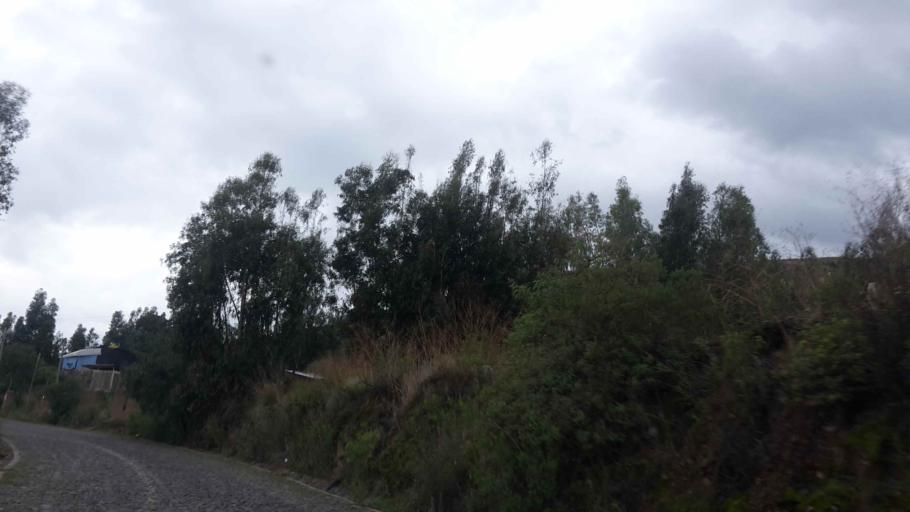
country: BO
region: Cochabamba
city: Cochabamba
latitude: -17.3734
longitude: -66.0556
